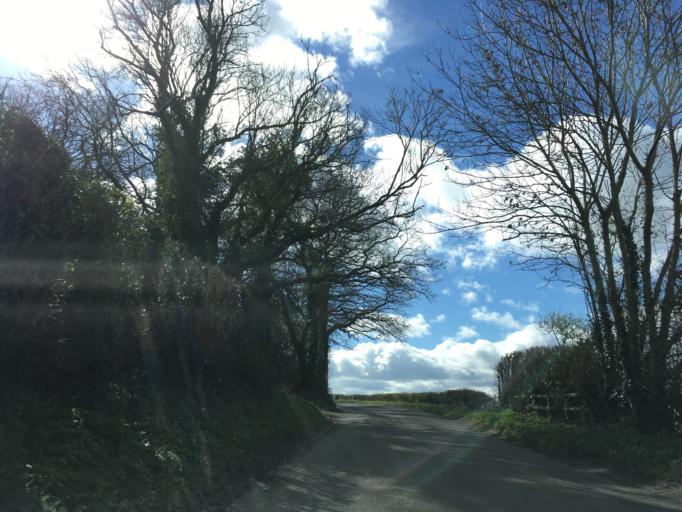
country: GB
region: England
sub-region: Gloucestershire
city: Wotton-under-Edge
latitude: 51.6006
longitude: -2.3346
